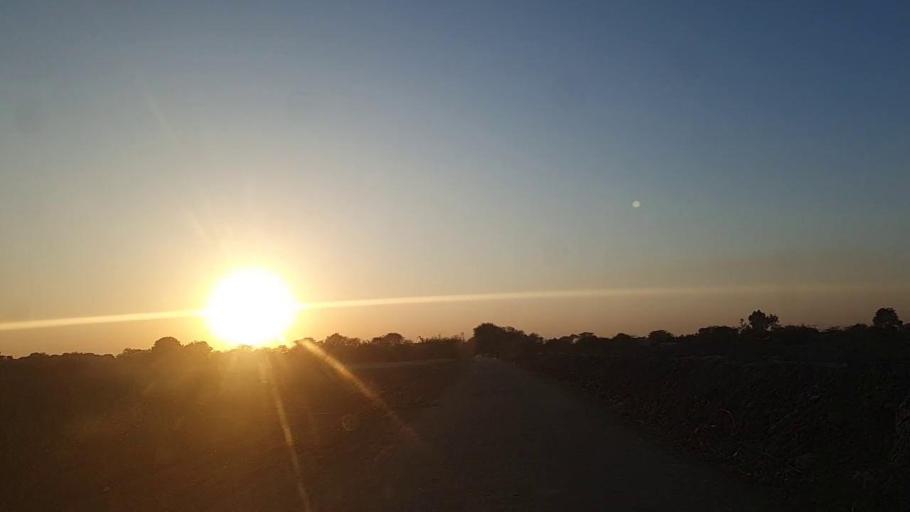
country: PK
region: Sindh
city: Naukot
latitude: 25.0563
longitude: 69.4009
